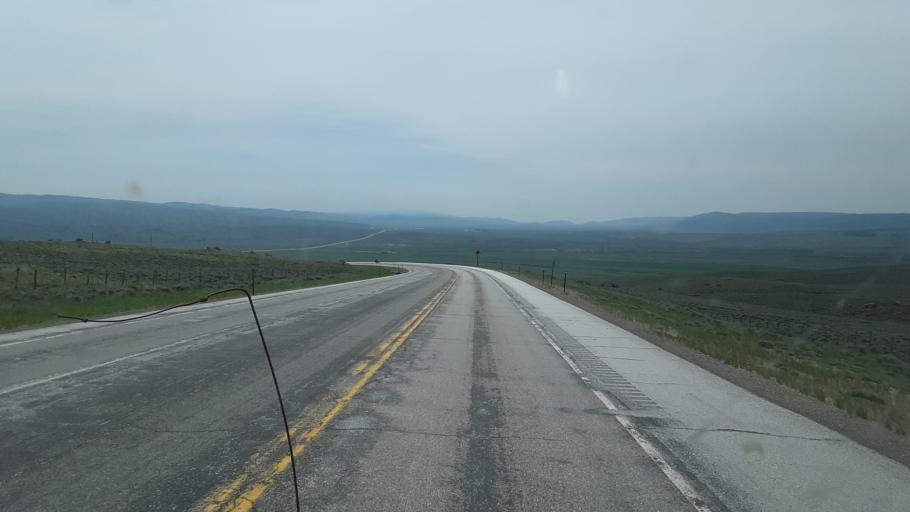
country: US
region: Wyoming
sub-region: Carbon County
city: Saratoga
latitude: 41.1304
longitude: -106.5659
